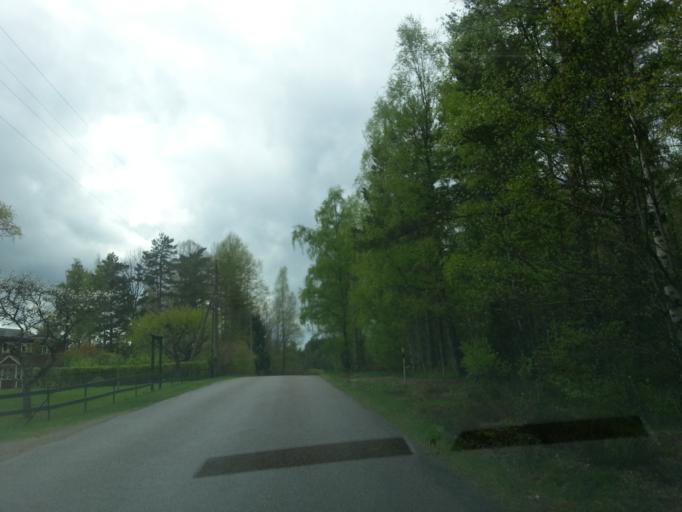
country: SE
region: OEstergoetland
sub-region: Norrkopings Kommun
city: Jursla
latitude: 58.6825
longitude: 16.2263
